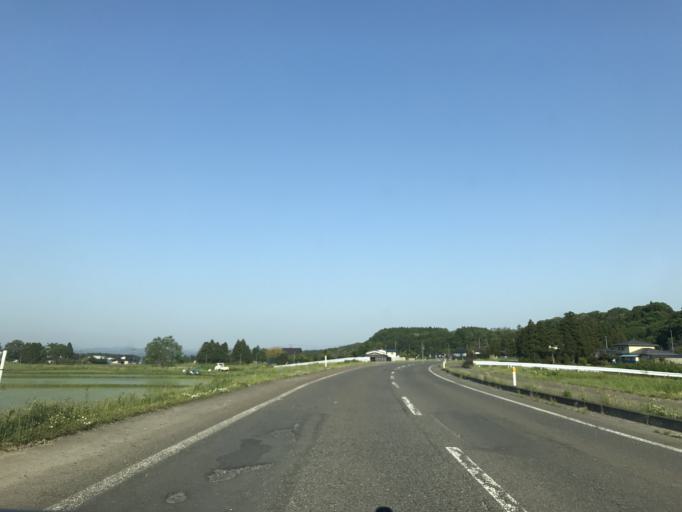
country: JP
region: Iwate
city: Kitakami
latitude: 39.2841
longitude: 141.0164
